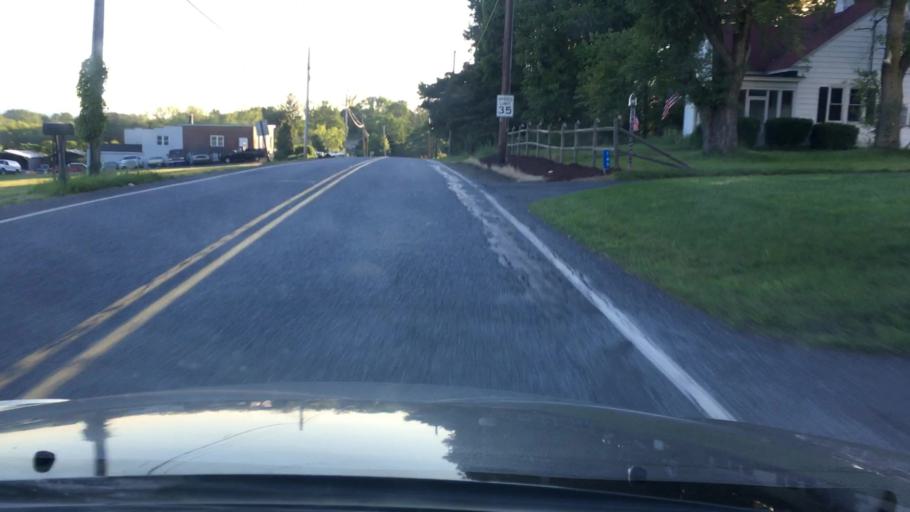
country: US
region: Pennsylvania
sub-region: Luzerne County
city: Harleigh
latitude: 41.0210
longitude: -75.9770
